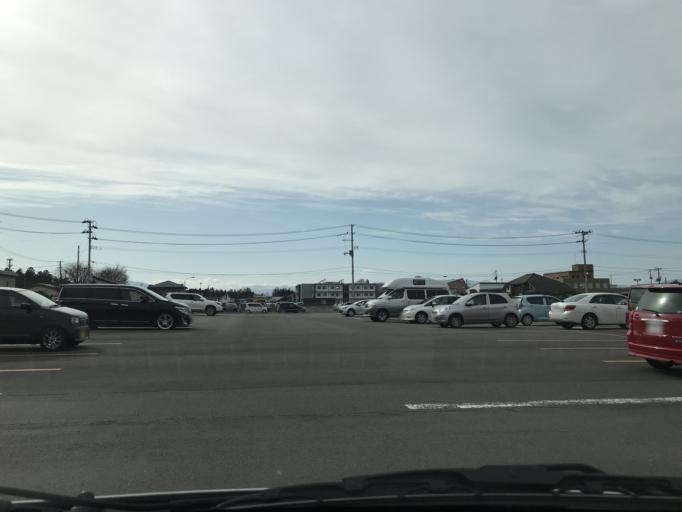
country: JP
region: Iwate
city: Kitakami
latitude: 39.2927
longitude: 141.0926
